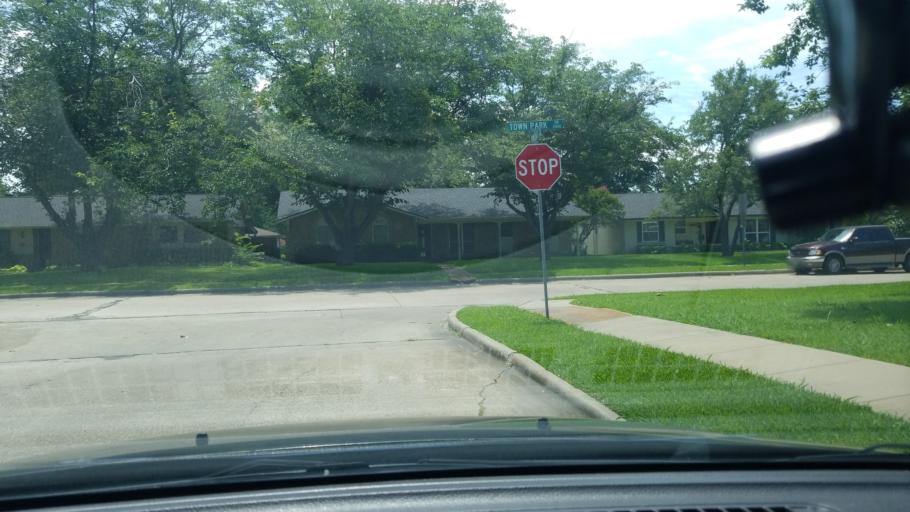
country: US
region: Texas
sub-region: Dallas County
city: Mesquite
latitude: 32.8081
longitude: -96.6519
